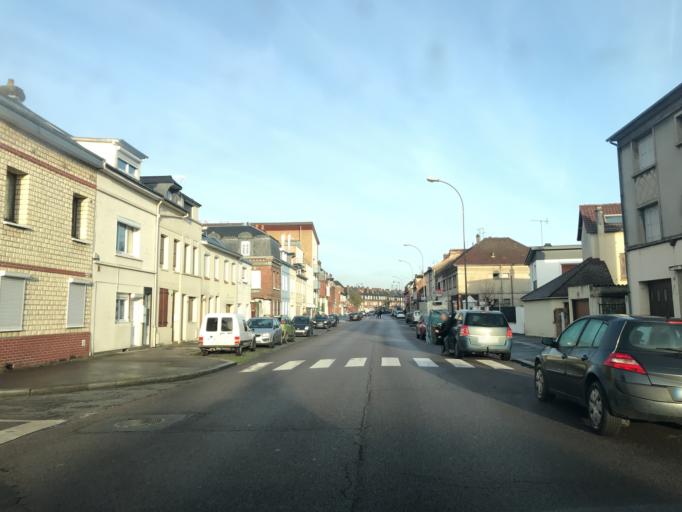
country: FR
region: Haute-Normandie
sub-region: Departement de la Seine-Maritime
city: Sotteville-les-Rouen
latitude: 49.4220
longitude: 1.0919
